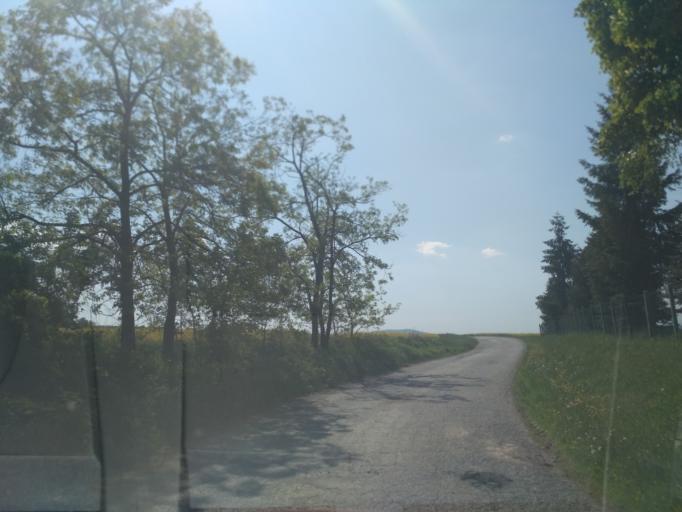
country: SK
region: Kosicky
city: Kosice
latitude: 48.8513
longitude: 21.4280
